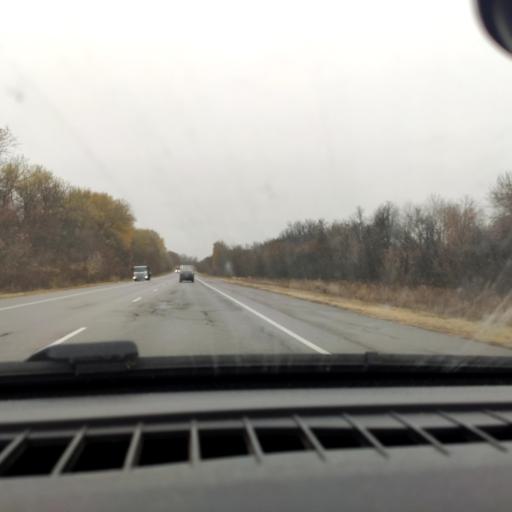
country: RU
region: Voronezj
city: Kolodeznyy
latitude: 51.2800
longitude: 39.0440
